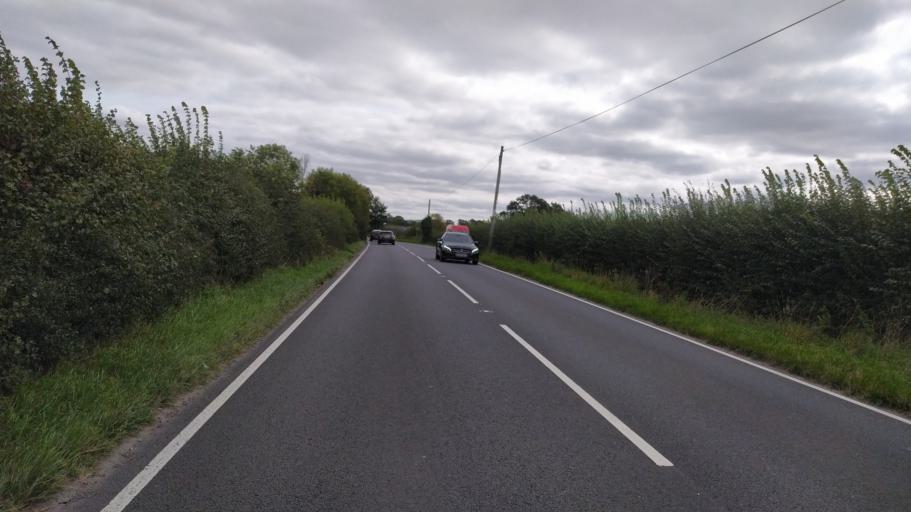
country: GB
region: England
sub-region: Dorset
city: Gillingham
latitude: 51.0243
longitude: -2.2522
